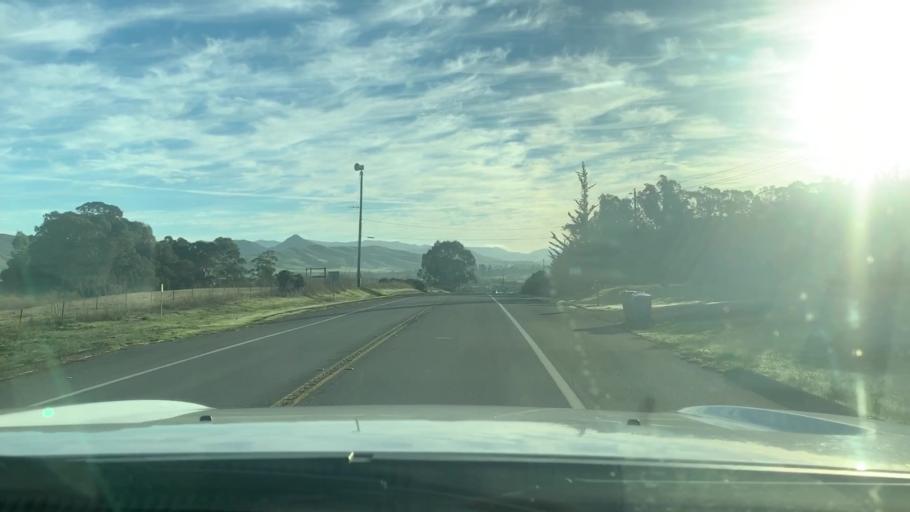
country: US
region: California
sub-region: San Luis Obispo County
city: Los Osos
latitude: 35.3026
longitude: -120.7970
